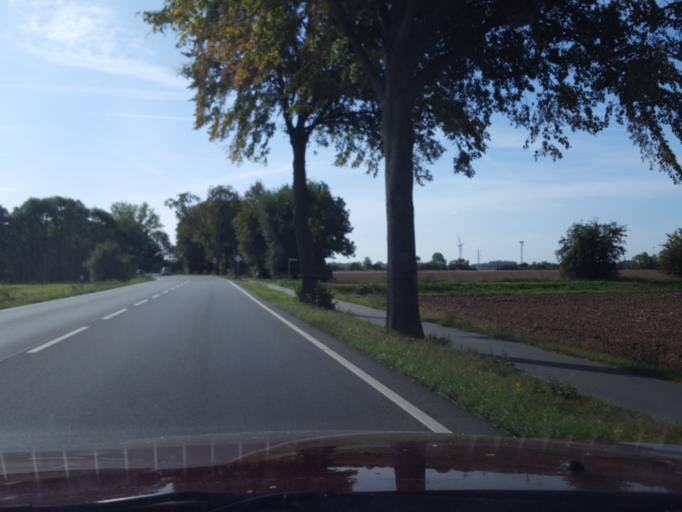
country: DE
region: Lower Saxony
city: Verden
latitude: 52.9001
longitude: 9.2172
